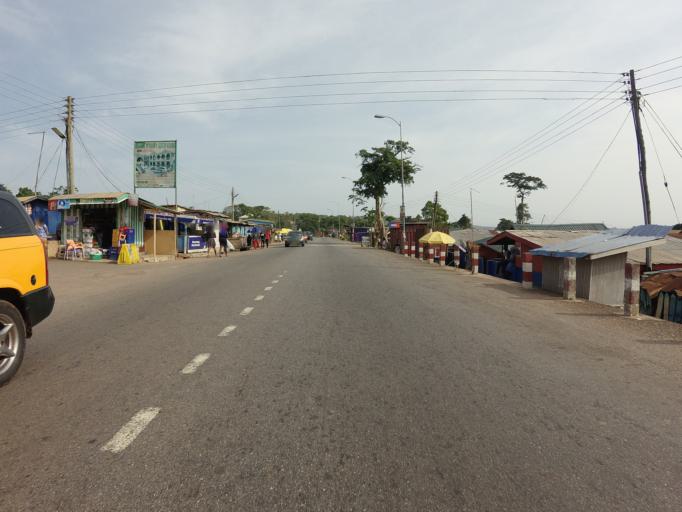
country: GH
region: Eastern
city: Aburi
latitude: 5.8190
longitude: -0.1865
